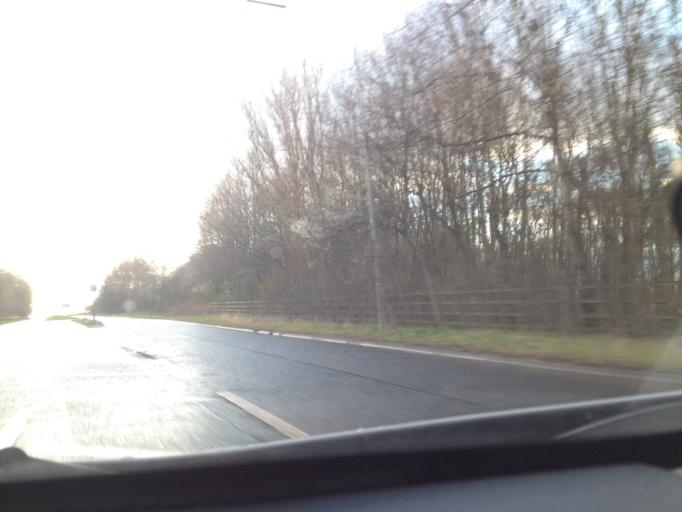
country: GB
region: Scotland
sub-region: South Lanarkshire
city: Larkhall
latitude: 55.7535
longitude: -3.9707
